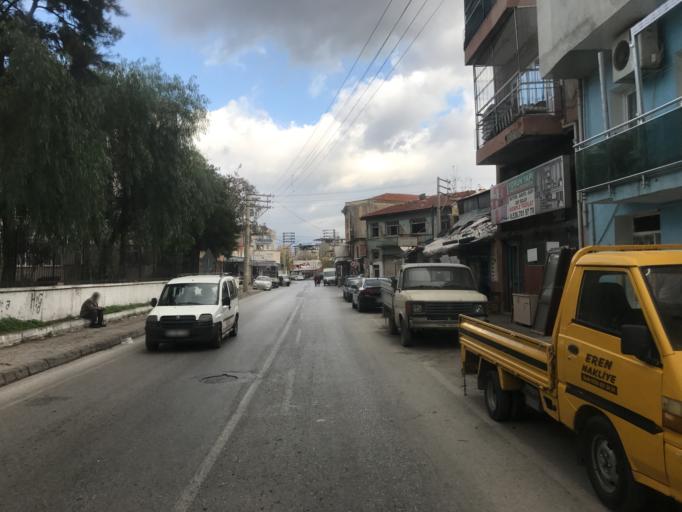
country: TR
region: Izmir
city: Izmir
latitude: 38.4195
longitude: 27.1579
